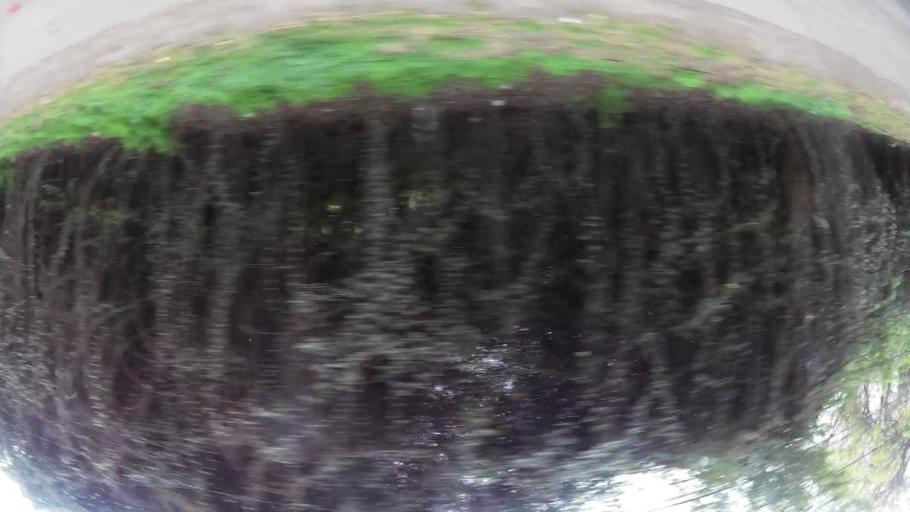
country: CL
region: Santiago Metropolitan
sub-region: Provincia de Chacabuco
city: Lampa
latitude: -33.2284
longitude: -70.7825
